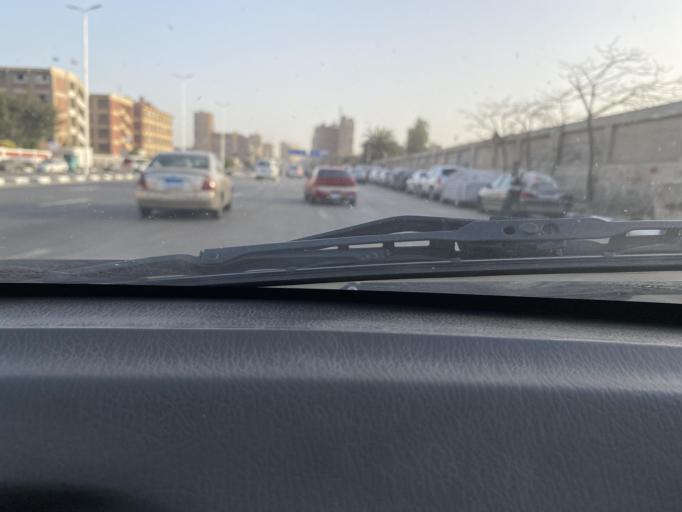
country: EG
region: Muhafazat al Qahirah
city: Cairo
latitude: 30.1175
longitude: 31.2966
